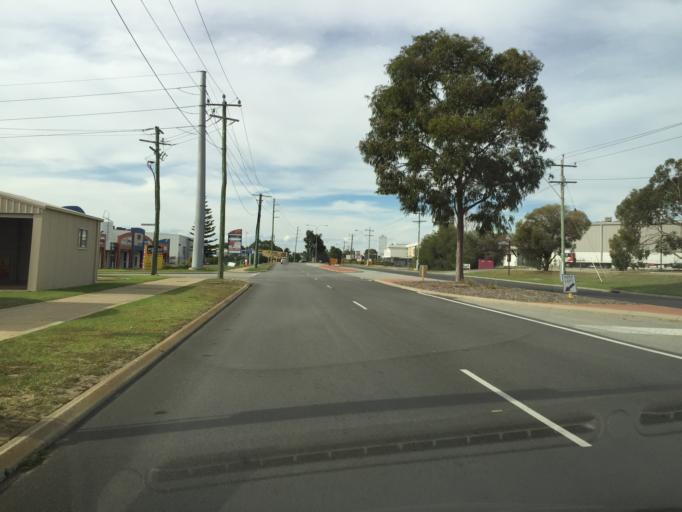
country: AU
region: Western Australia
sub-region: Canning
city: Canning Vale
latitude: -32.0618
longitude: 115.9050
